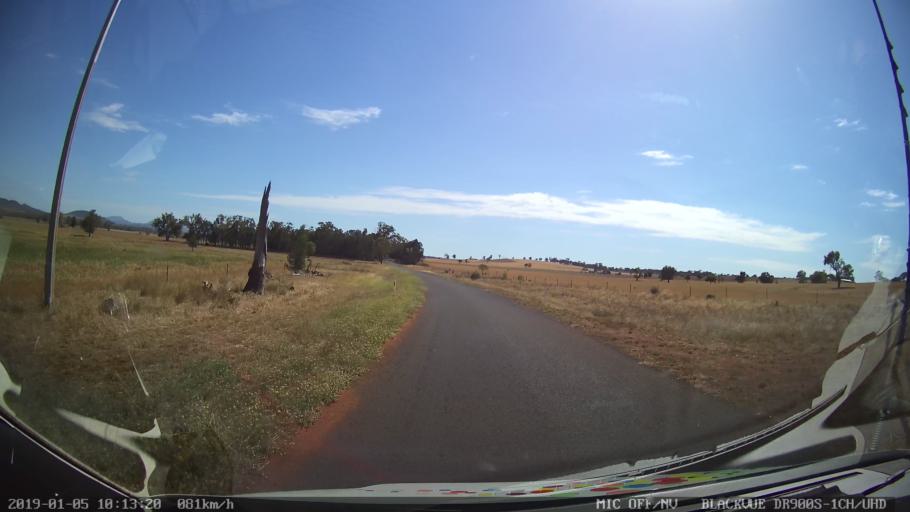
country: AU
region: New South Wales
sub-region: Gilgandra
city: Gilgandra
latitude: -31.6030
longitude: 148.9237
